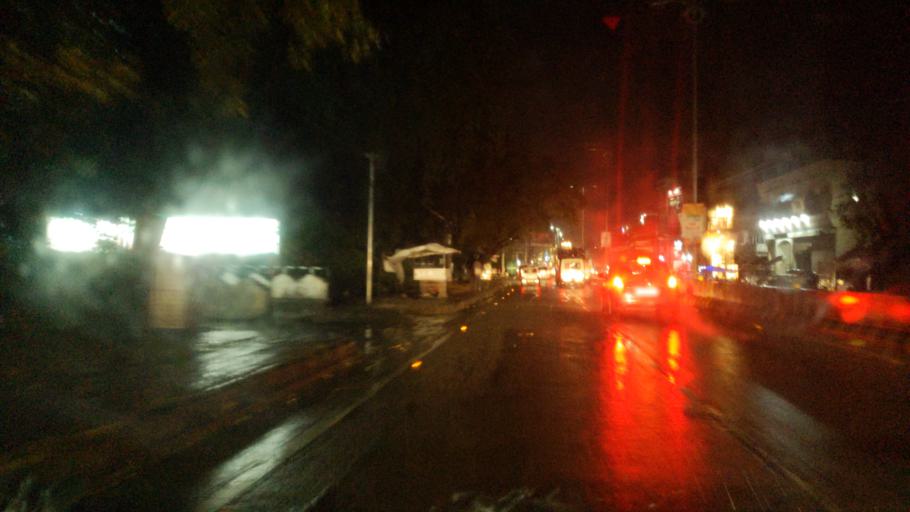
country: IN
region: Uttarakhand
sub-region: Naini Tal
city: Haldwani
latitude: 29.2473
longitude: 79.5381
